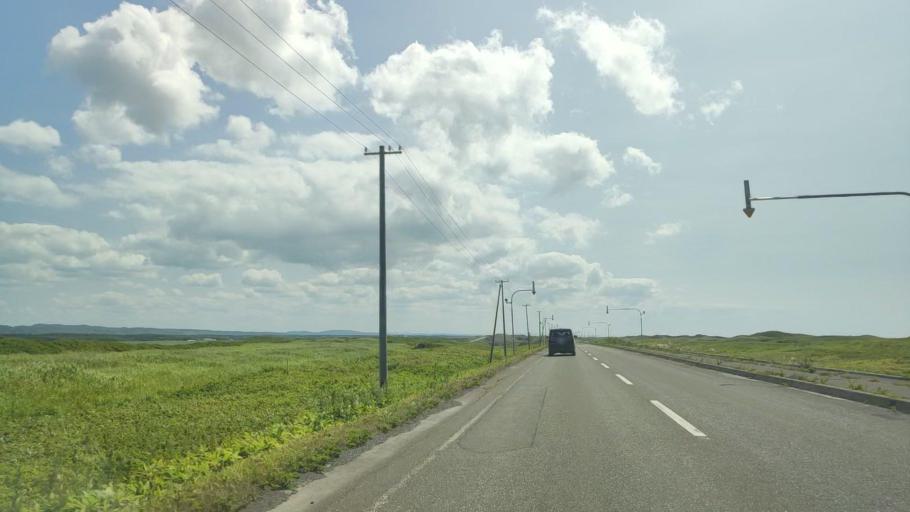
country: JP
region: Hokkaido
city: Makubetsu
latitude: 44.9460
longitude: 141.7128
